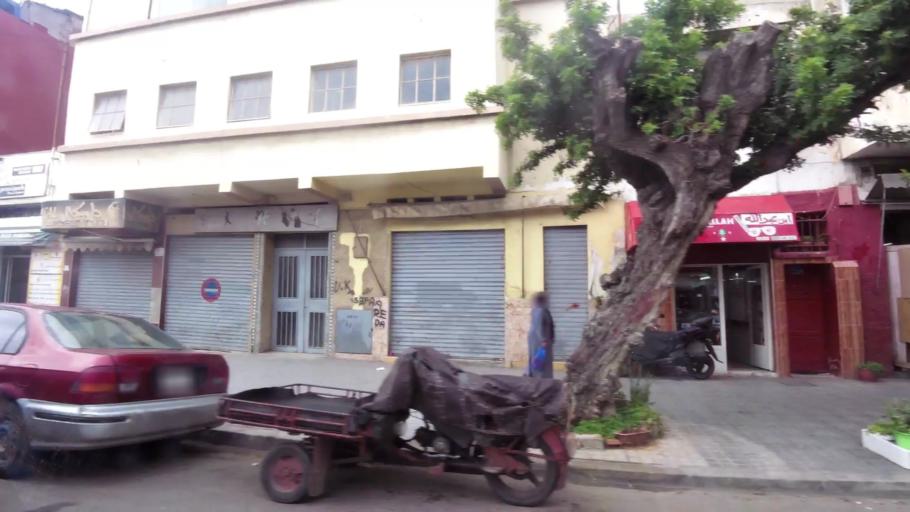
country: MA
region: Grand Casablanca
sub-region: Casablanca
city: Casablanca
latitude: 33.6004
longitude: -7.6311
